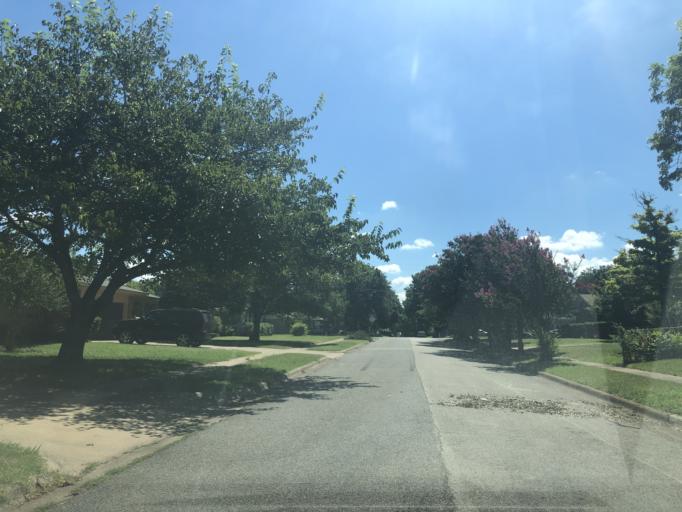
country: US
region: Texas
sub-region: Dallas County
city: Duncanville
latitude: 32.6554
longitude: -96.9138
